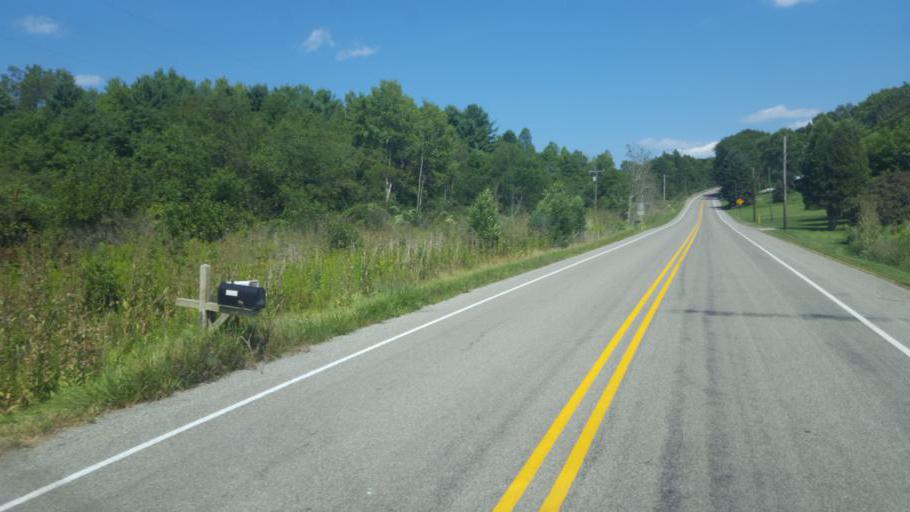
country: US
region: Pennsylvania
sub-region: Clarion County
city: Knox
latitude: 41.1079
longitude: -79.6217
